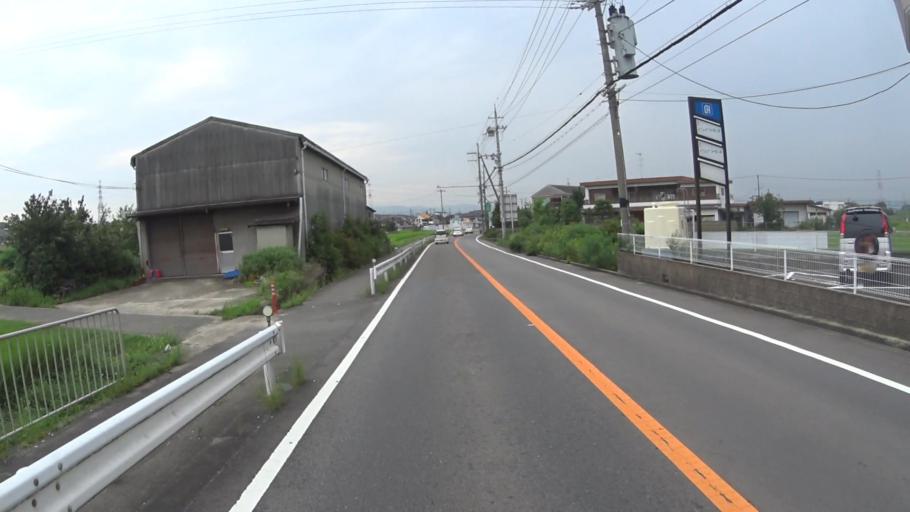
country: JP
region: Kyoto
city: Tanabe
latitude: 34.8250
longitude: 135.7606
